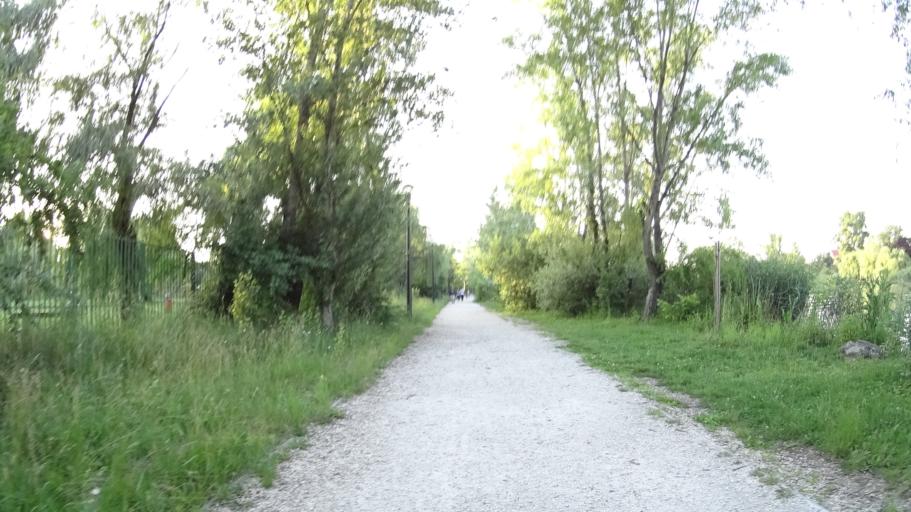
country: HU
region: Budapest
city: Budapest XXIII. keruelet
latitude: 47.4055
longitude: 19.1026
